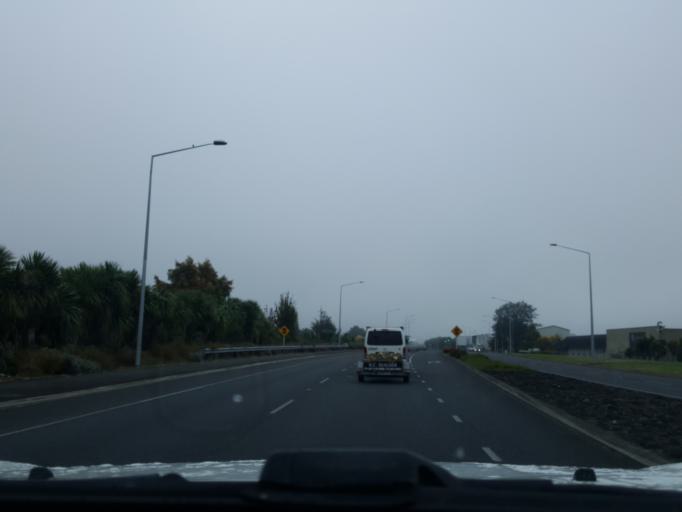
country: NZ
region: Waikato
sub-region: Hamilton City
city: Hamilton
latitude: -37.7642
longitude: 175.2352
